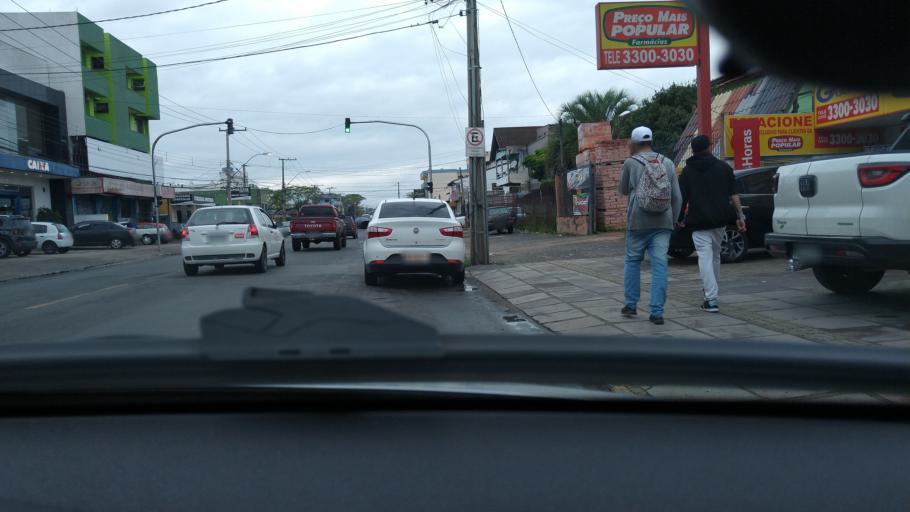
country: BR
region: Rio Grande do Sul
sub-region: Canoas
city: Canoas
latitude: -29.9026
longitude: -51.1944
